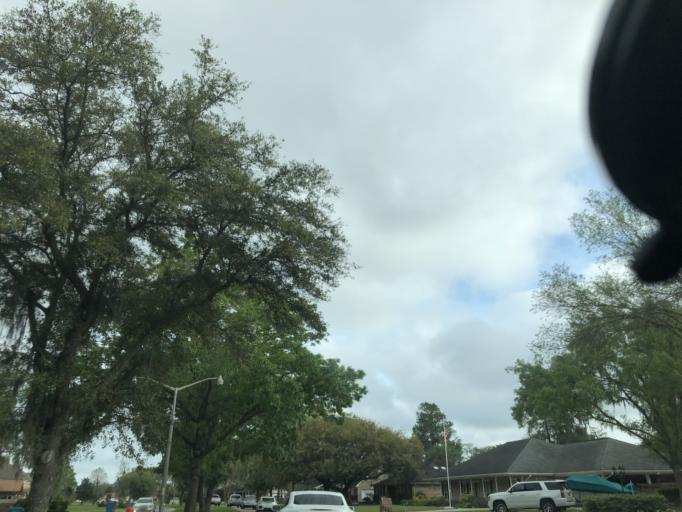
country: US
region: Louisiana
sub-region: Saint Charles Parish
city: New Sarpy
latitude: 29.9801
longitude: -90.3628
